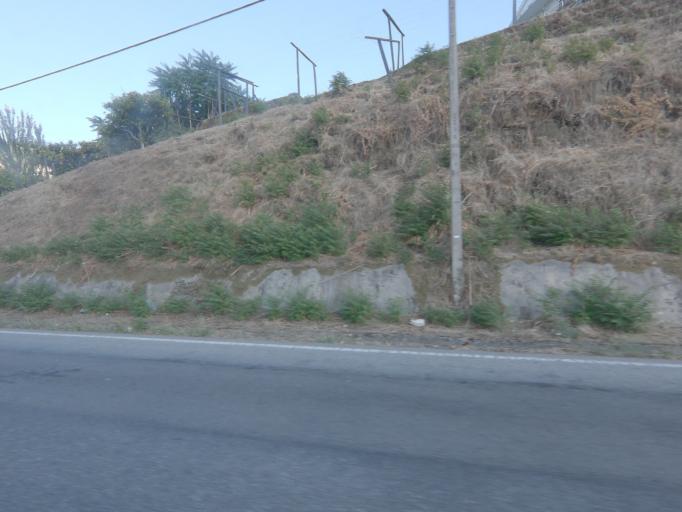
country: PT
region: Viseu
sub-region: Armamar
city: Armamar
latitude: 41.1530
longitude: -7.6793
